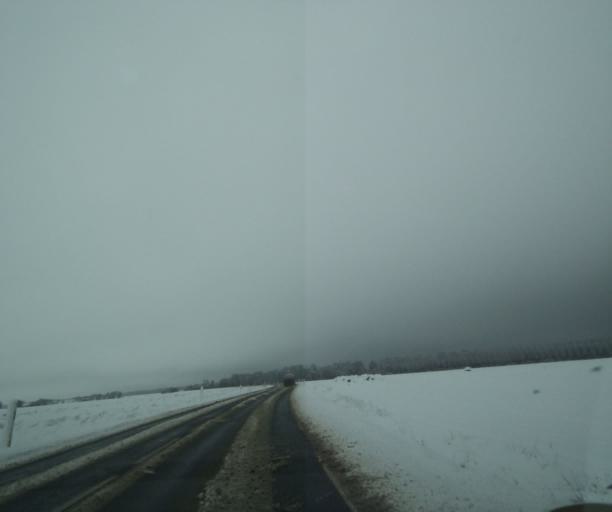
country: FR
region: Champagne-Ardenne
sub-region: Departement de la Haute-Marne
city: Wassy
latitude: 48.5630
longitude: 4.9224
